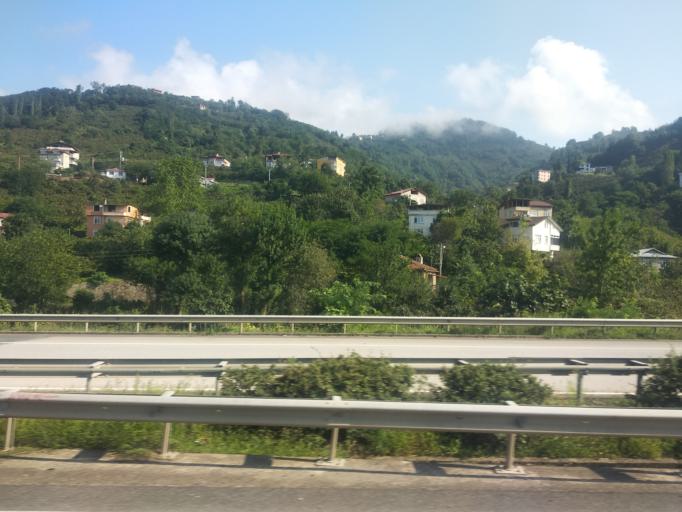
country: TR
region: Ordu
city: Ordu
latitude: 41.0158
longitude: 37.8420
